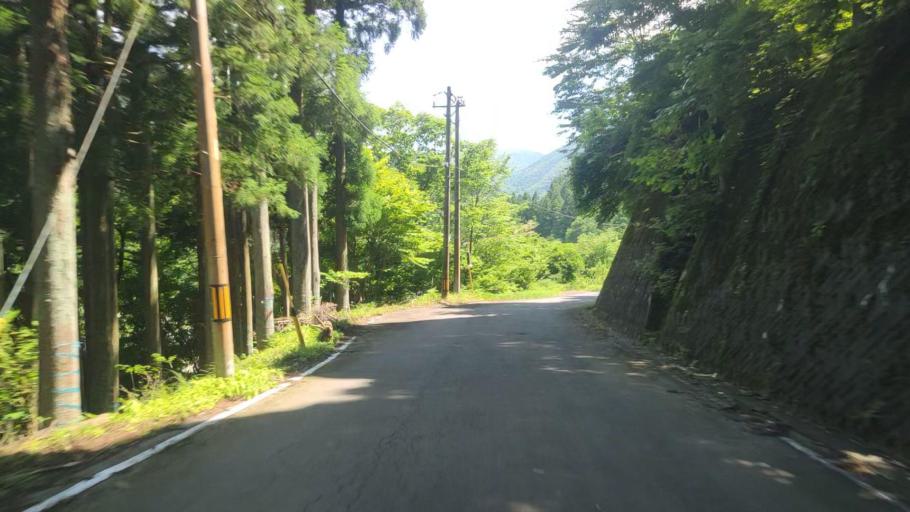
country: JP
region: Fukui
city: Ono
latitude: 35.7186
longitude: 136.5838
